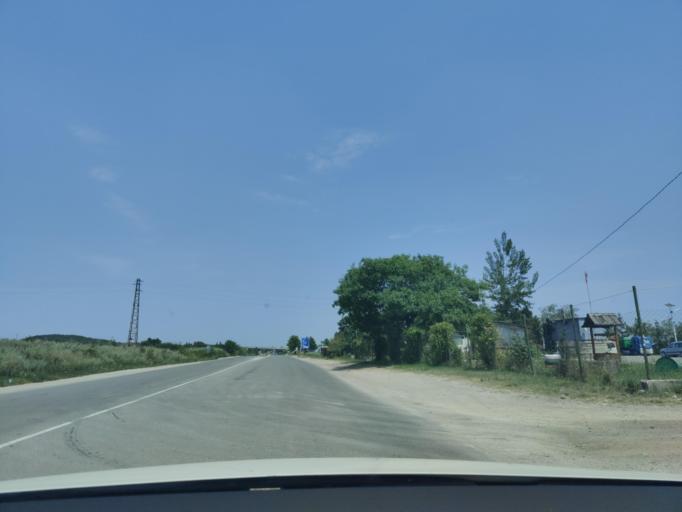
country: BG
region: Montana
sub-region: Obshtina Montana
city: Montana
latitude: 43.4310
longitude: 23.2314
